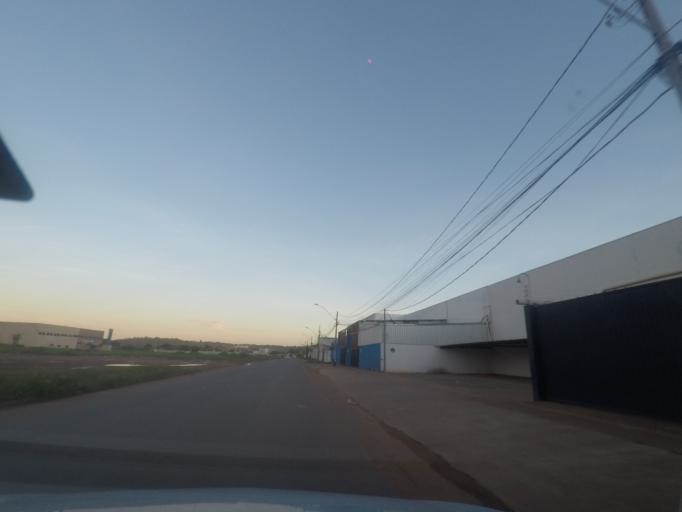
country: BR
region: Goias
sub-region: Goiania
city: Goiania
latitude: -16.6938
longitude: -49.3331
